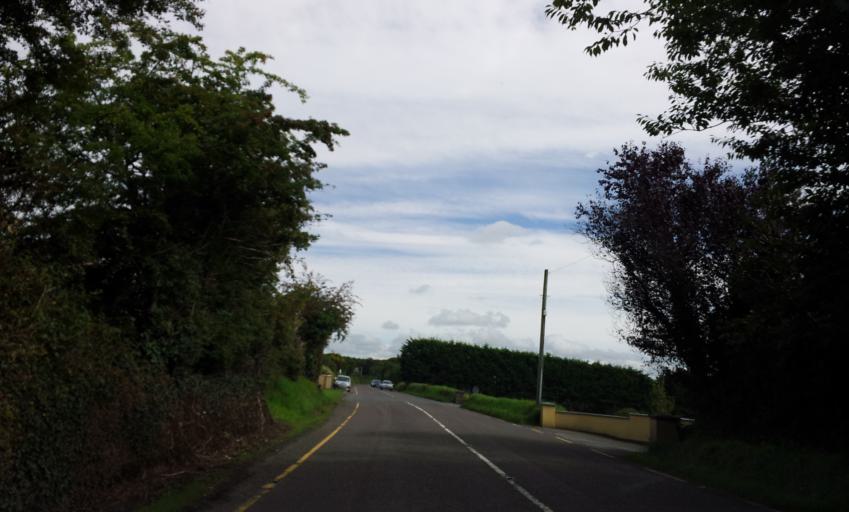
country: IE
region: Munster
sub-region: Ciarrai
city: Killorglin
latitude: 52.1014
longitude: -9.7712
